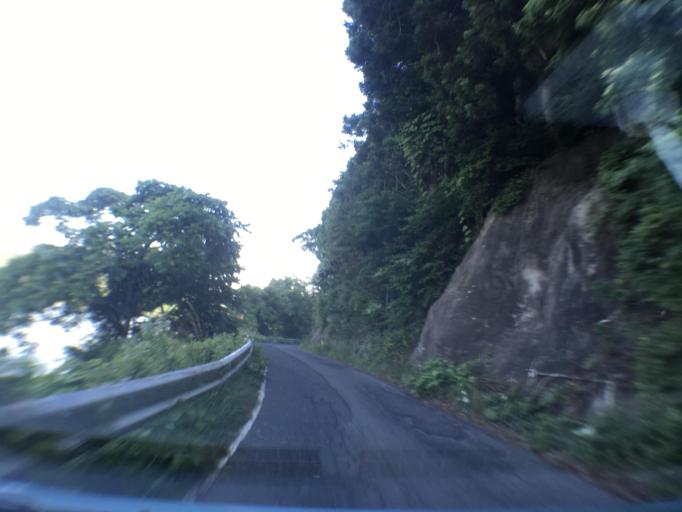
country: JP
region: Miyagi
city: Wakuya
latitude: 38.6314
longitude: 141.2872
